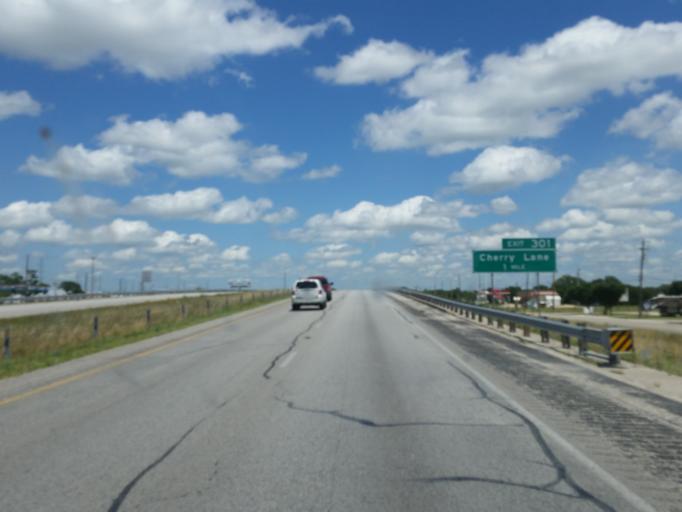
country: US
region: Texas
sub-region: Callahan County
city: Clyde
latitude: 32.4156
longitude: -99.5108
